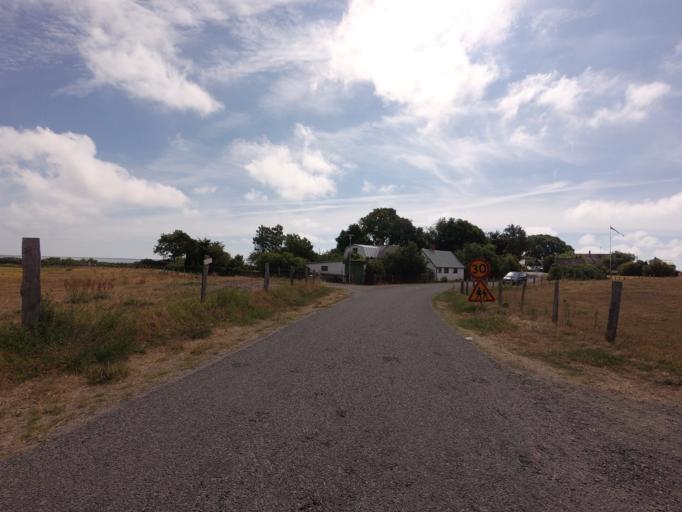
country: SE
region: Skane
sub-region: Simrishamns Kommun
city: Simrishamn
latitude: 55.4878
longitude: 14.3141
